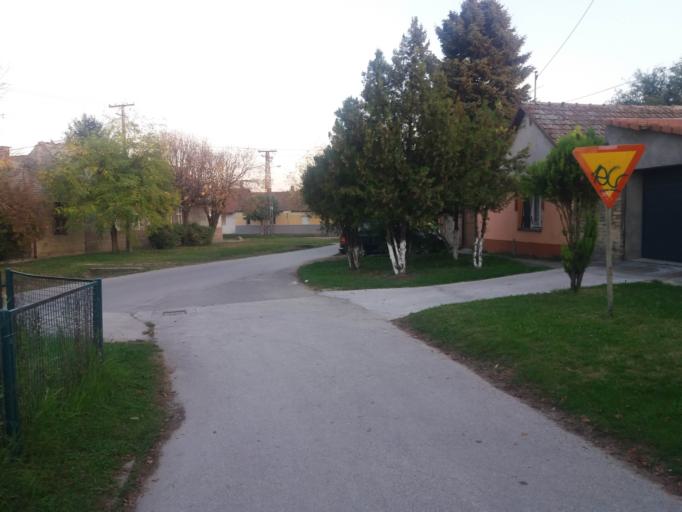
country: RS
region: Autonomna Pokrajina Vojvodina
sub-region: Severnobacki Okrug
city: Subotica
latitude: 46.1038
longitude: 19.6461
